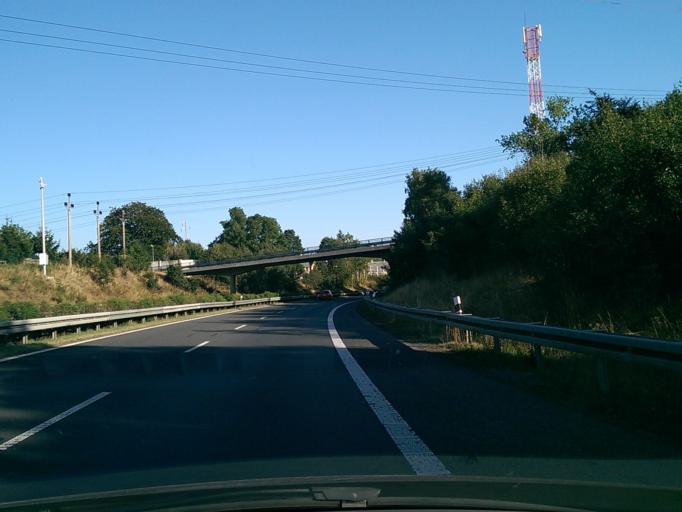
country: CZ
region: Liberecky
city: Hodkovice nad Mohelkou
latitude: 50.7083
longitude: 15.0894
